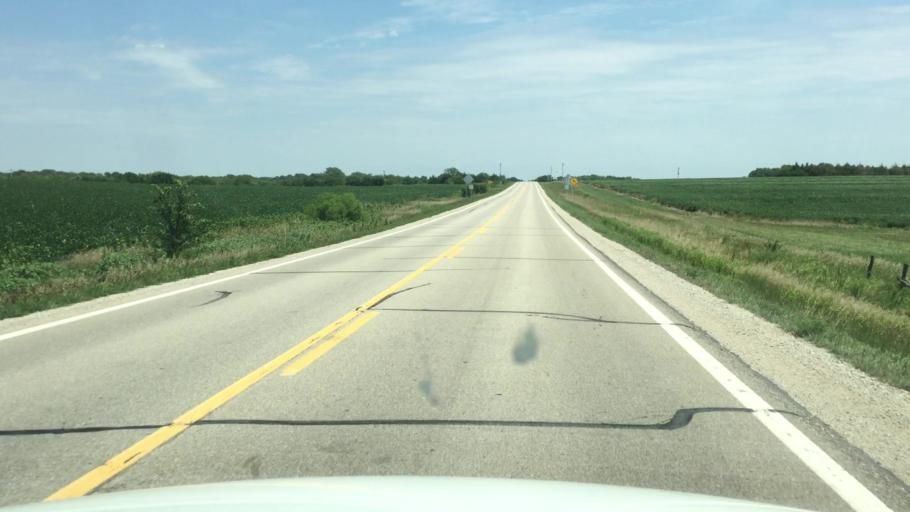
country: US
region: Kansas
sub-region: Osage County
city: Overbrook
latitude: 38.9713
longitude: -95.4878
